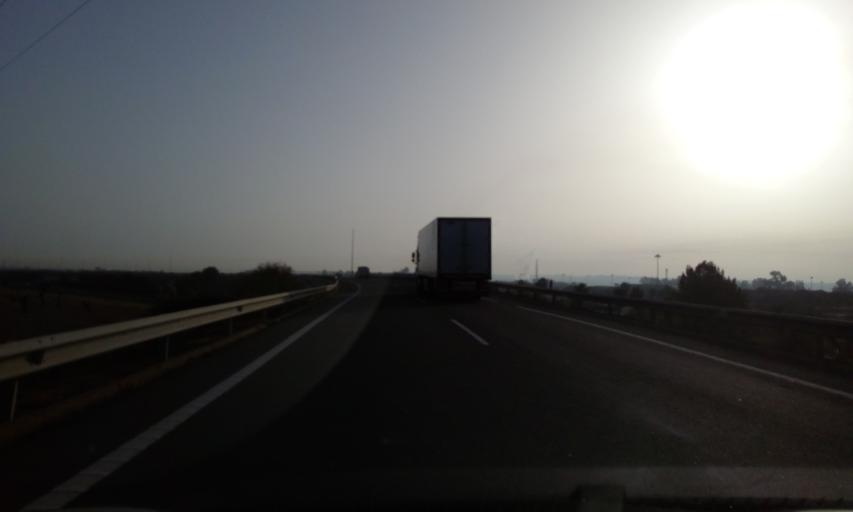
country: ES
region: Andalusia
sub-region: Provincia de Huelva
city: San Juan del Puerto
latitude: 37.3122
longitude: -6.8813
